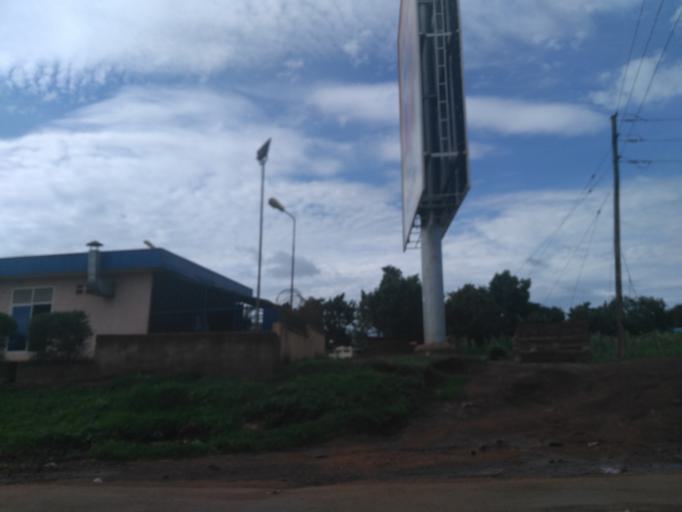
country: UG
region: Eastern Region
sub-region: Jinja District
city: Jinja
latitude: 0.4416
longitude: 33.2105
